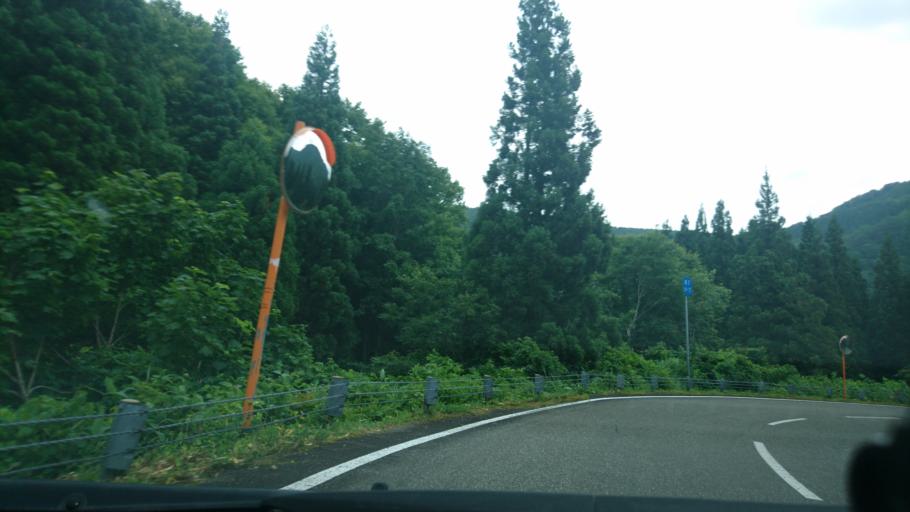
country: JP
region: Akita
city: Yuzawa
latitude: 39.1617
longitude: 140.7459
